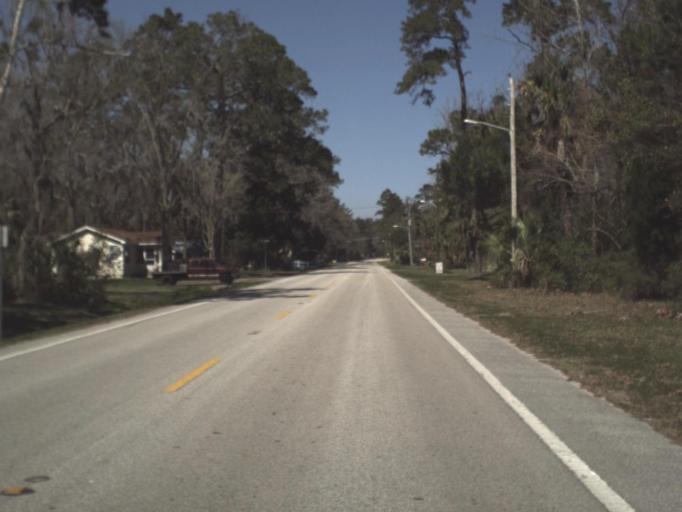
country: US
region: Florida
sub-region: Leon County
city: Woodville
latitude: 30.1592
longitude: -84.2053
